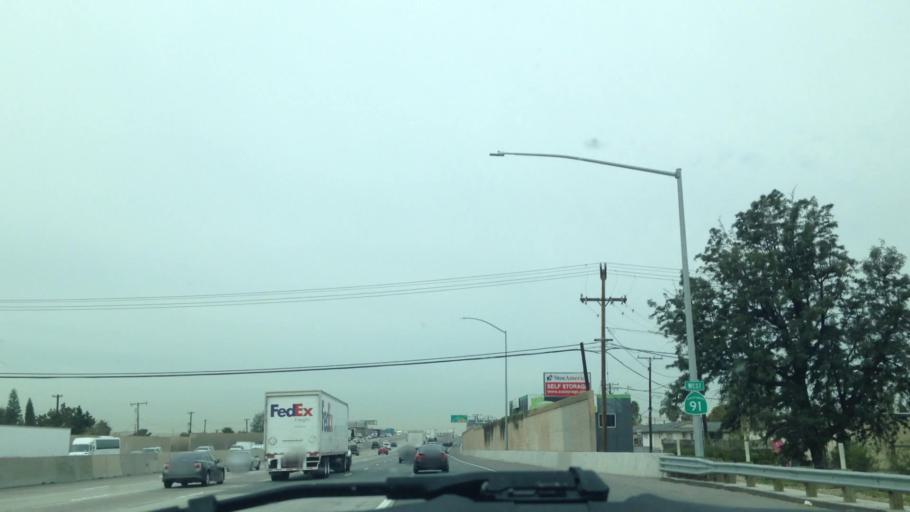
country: US
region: California
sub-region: Orange County
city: Placentia
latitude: 33.8544
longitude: -117.8929
